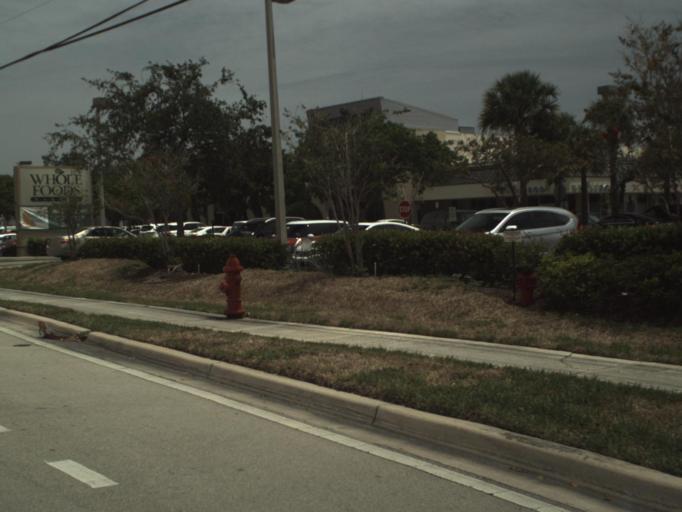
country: US
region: Florida
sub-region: Broward County
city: Sunrise
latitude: 26.1532
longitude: -80.1185
